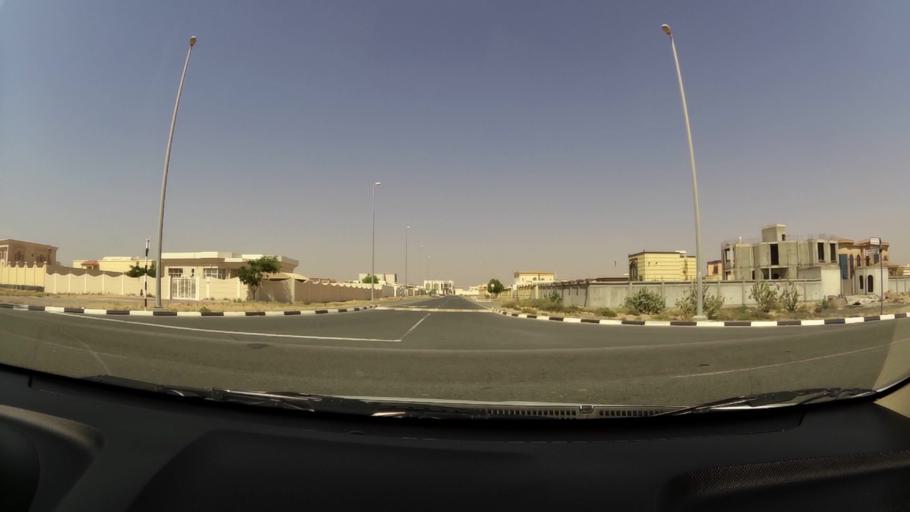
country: AE
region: Umm al Qaywayn
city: Umm al Qaywayn
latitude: 25.4896
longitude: 55.6005
